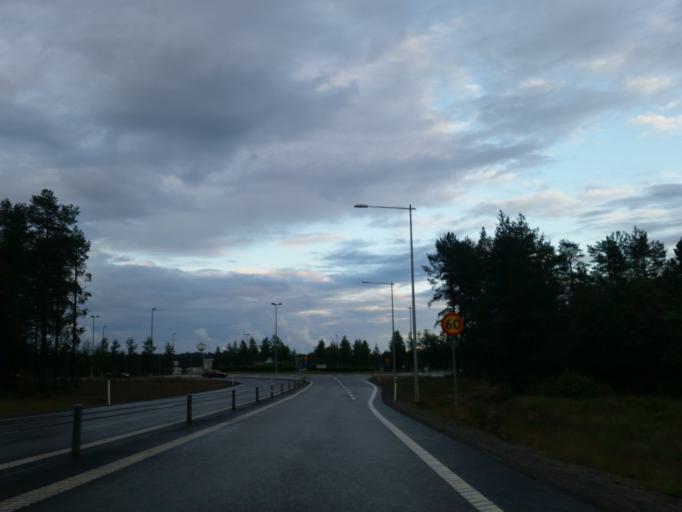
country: SE
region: Vaesterbotten
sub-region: Umea Kommun
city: Umea
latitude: 63.8503
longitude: 20.2933
